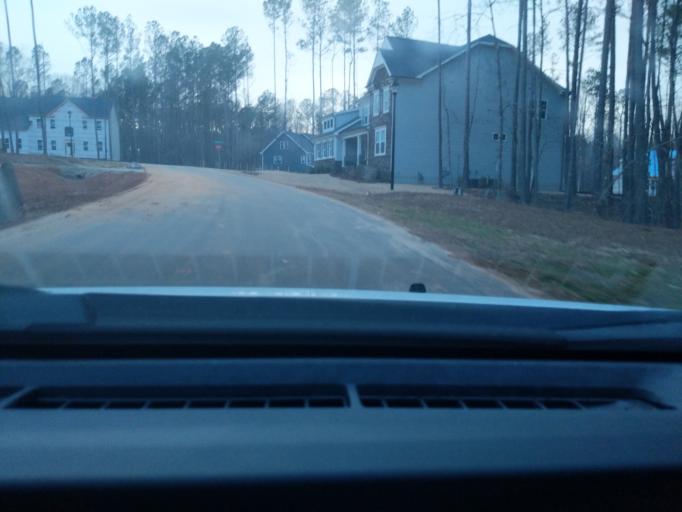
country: US
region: North Carolina
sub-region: Wake County
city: Garner
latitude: 35.7138
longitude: -78.6814
